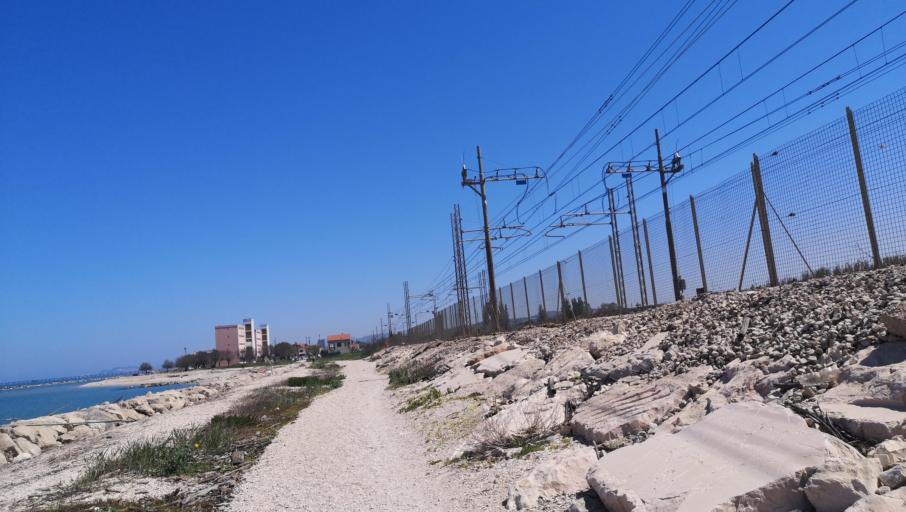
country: IT
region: The Marches
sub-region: Provincia di Ancona
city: Marina di Montemarciano
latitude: 43.6486
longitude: 13.3534
